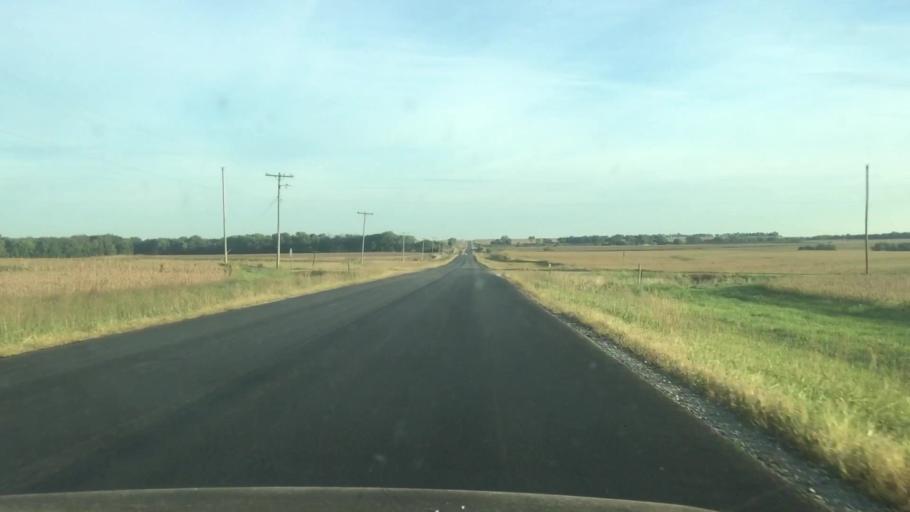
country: US
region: Kansas
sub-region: Marshall County
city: Marysville
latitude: 39.8701
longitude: -96.6007
